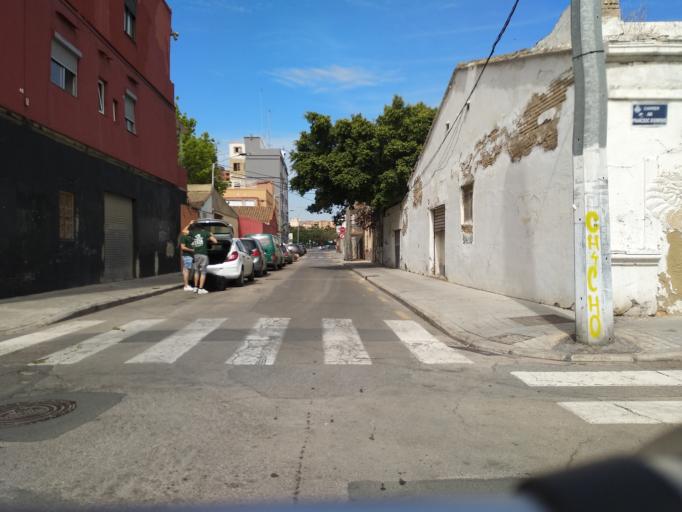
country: ES
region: Valencia
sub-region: Provincia de Valencia
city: Alboraya
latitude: 39.4700
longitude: -0.3327
